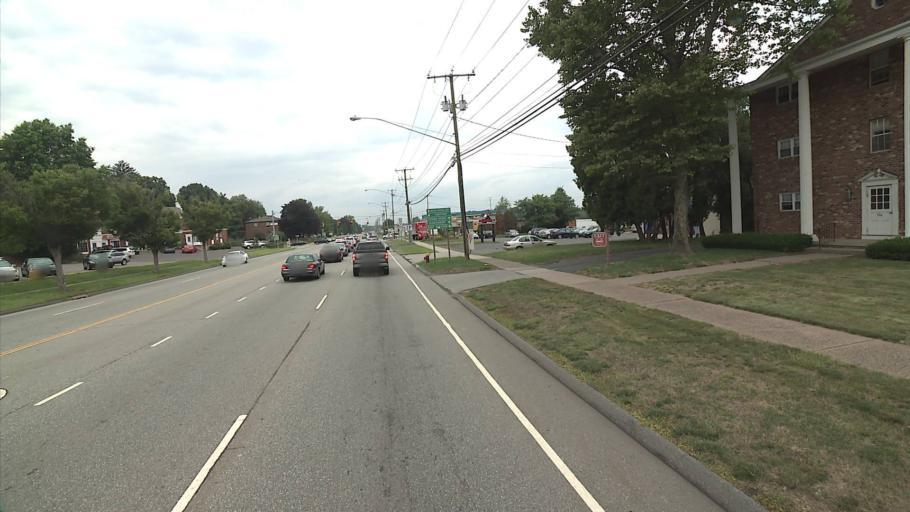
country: US
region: Connecticut
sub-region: Hartford County
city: Wethersfield
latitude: 41.6969
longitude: -72.6578
